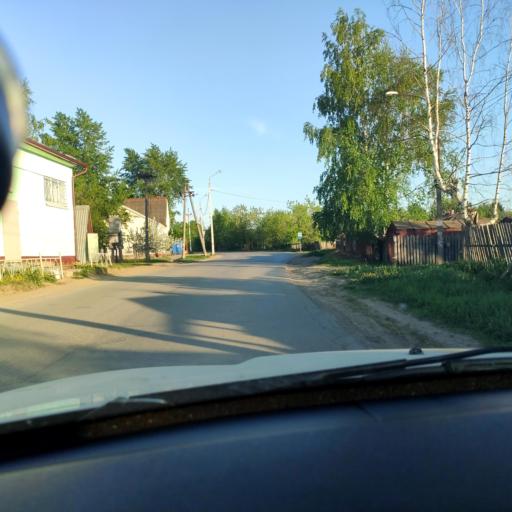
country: RU
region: Perm
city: Polazna
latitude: 58.1453
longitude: 56.4479
